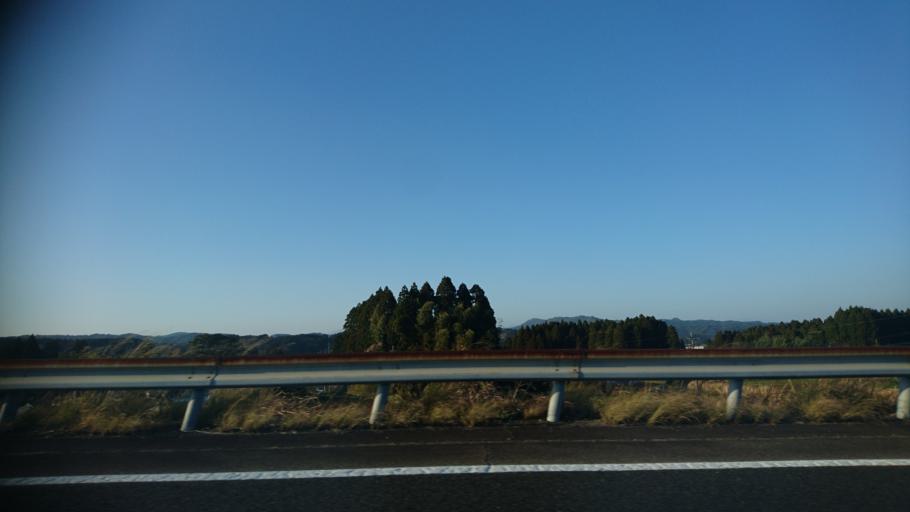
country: JP
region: Miyazaki
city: Miyazaki-shi
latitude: 31.8202
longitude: 131.2799
